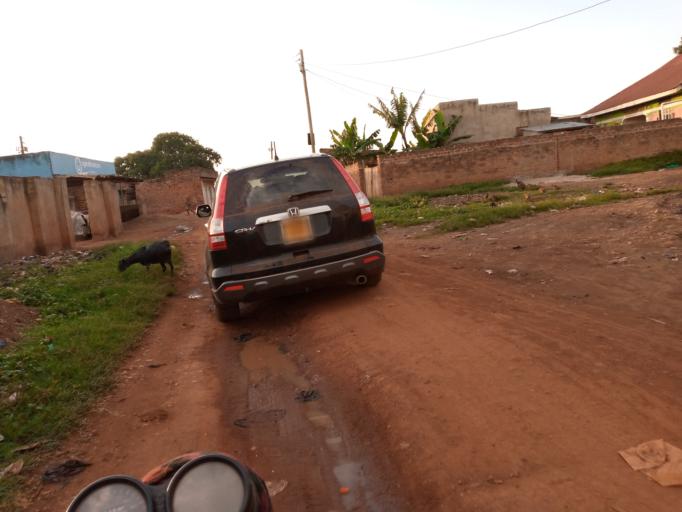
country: UG
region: Eastern Region
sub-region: Mbale District
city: Mbale
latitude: 1.0800
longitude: 34.1536
